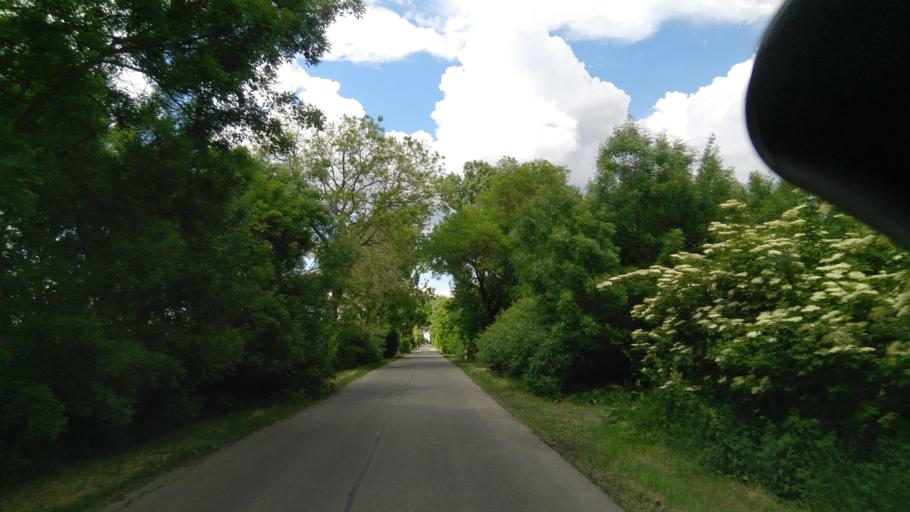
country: HU
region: Bekes
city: Bucsa
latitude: 47.1600
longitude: 21.0841
